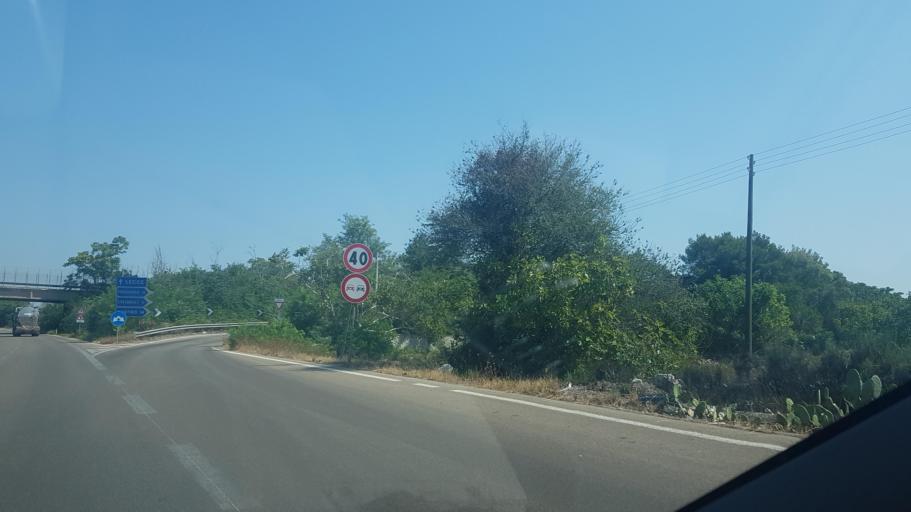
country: IT
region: Apulia
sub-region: Provincia di Lecce
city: Muro Leccese
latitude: 40.1156
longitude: 18.3209
